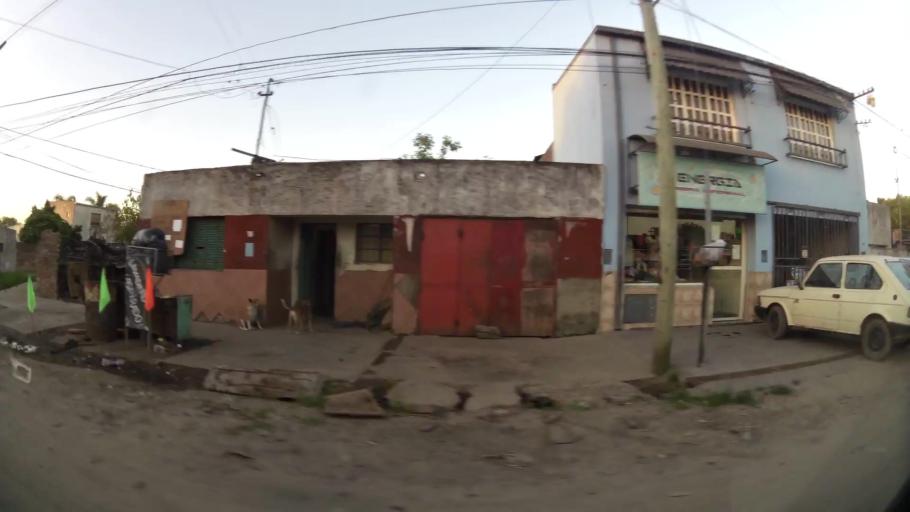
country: AR
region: Santa Fe
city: Santa Fe de la Vera Cruz
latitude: -31.5963
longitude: -60.6966
